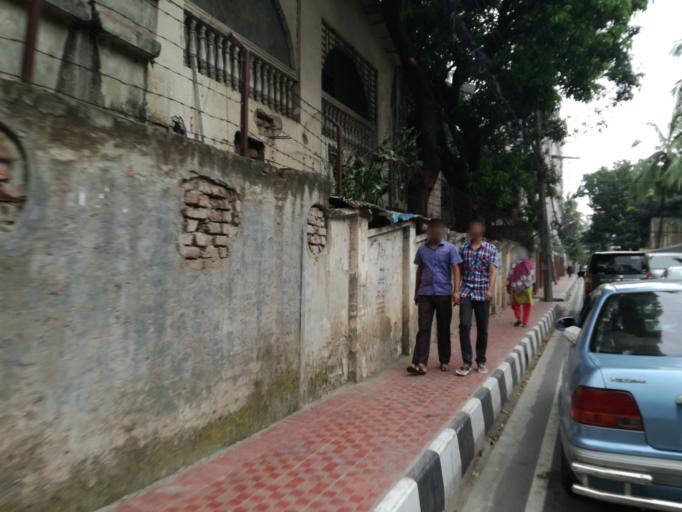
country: BD
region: Dhaka
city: Paltan
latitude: 23.7822
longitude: 90.4155
